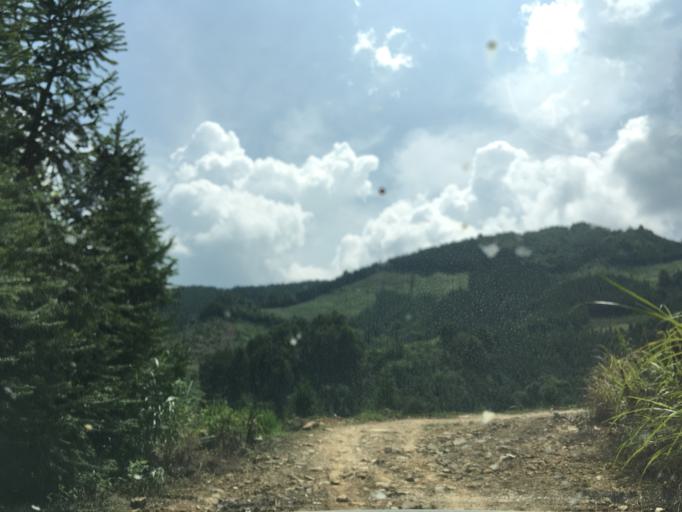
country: CN
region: Guangxi Zhuangzu Zizhiqu
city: Xinzhou
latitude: 24.9544
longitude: 105.7854
